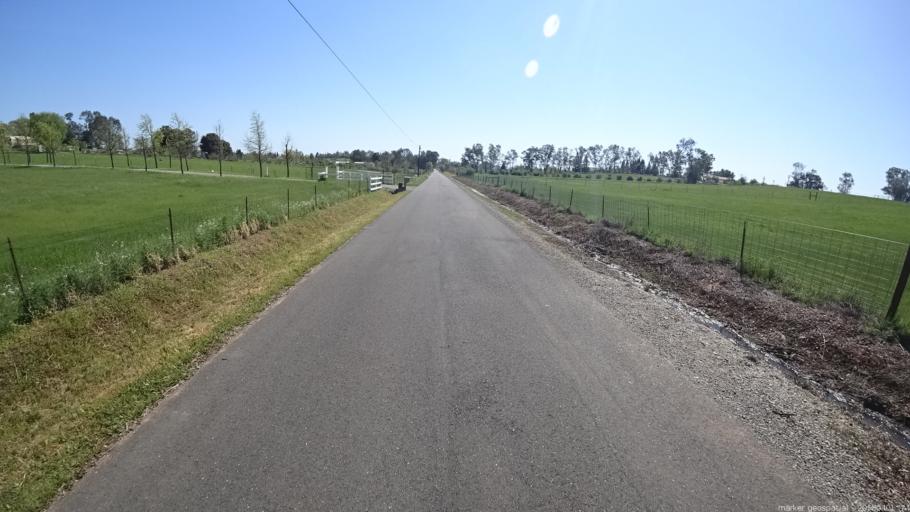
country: US
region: California
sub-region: Sacramento County
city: Wilton
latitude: 38.4137
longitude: -121.2456
